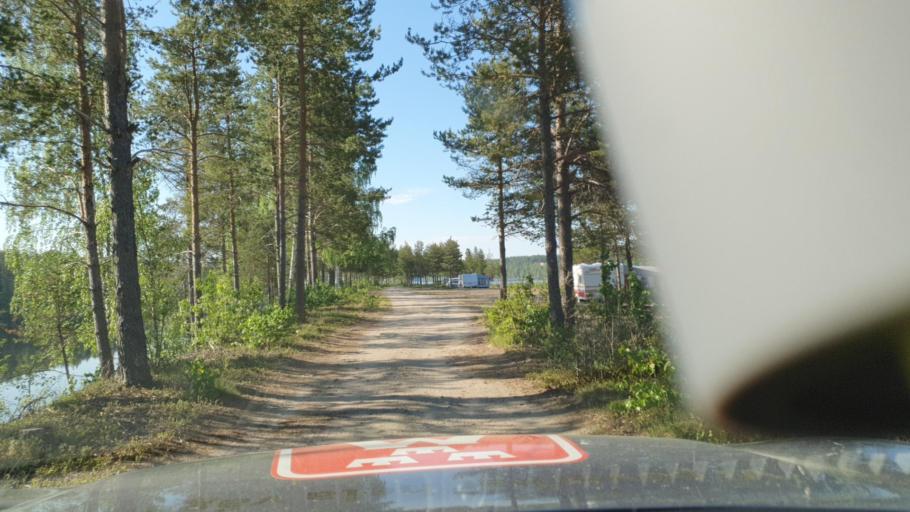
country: SE
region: Norrbotten
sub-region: Alvsbyns Kommun
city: AElvsbyn
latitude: 66.2187
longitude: 20.8603
